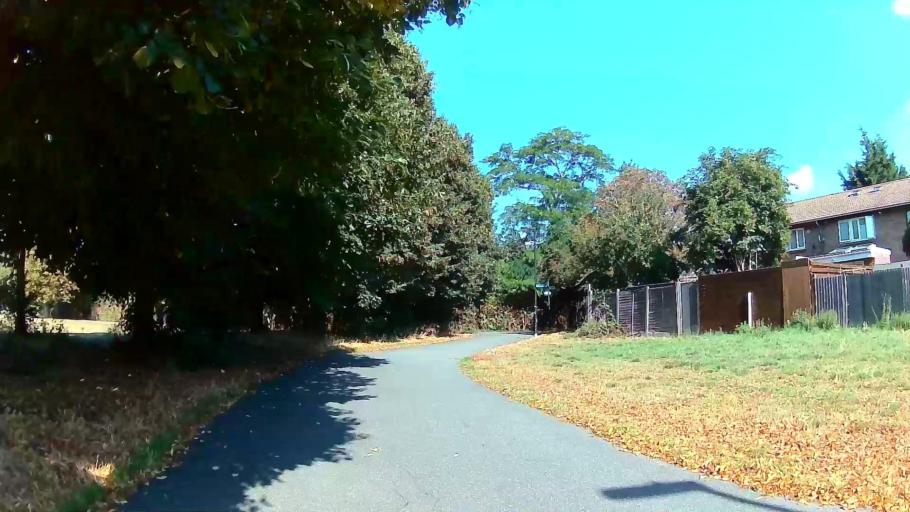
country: GB
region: England
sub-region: Greater London
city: Woolwich
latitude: 51.5102
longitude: 0.0550
